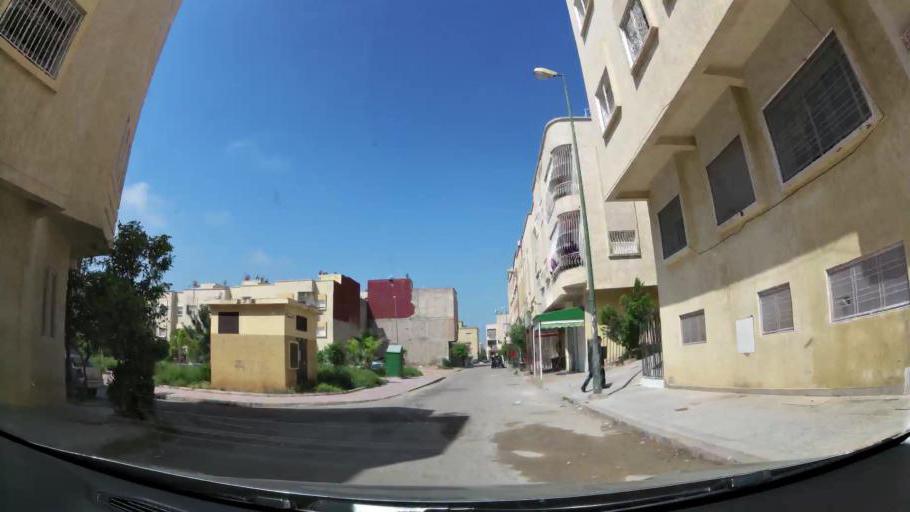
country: MA
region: Fes-Boulemane
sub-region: Fes
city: Fes
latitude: 34.0595
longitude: -5.0206
